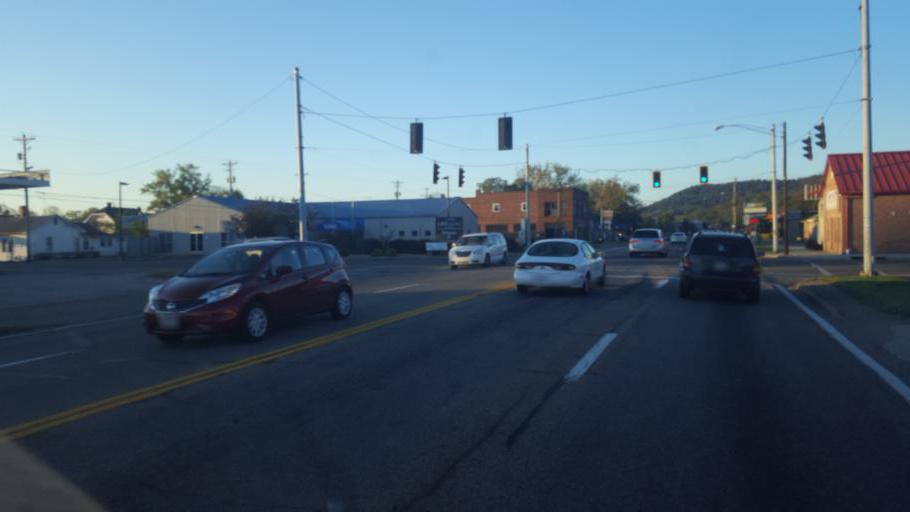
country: US
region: Ohio
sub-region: Scioto County
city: Lucasville
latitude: 38.8792
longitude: -82.9968
